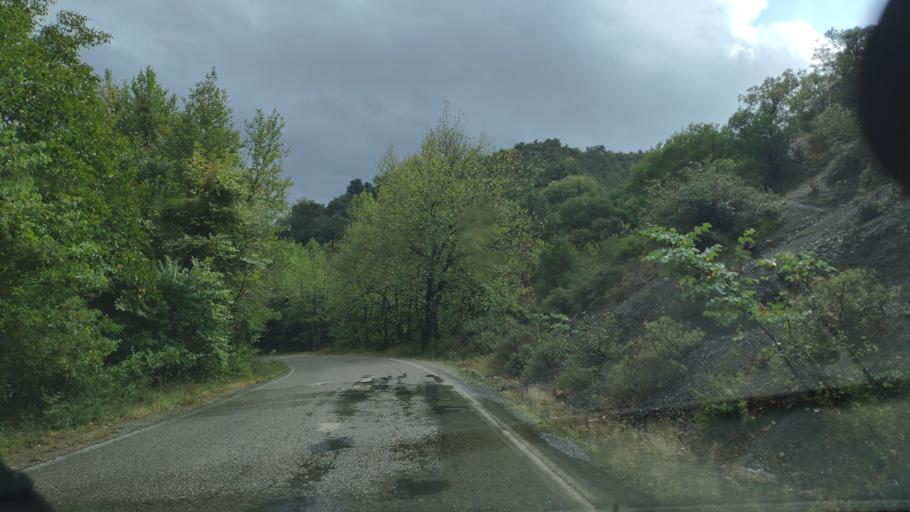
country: GR
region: West Greece
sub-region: Nomos Aitolias kai Akarnanias
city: Krikellos
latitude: 38.9604
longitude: 21.3338
